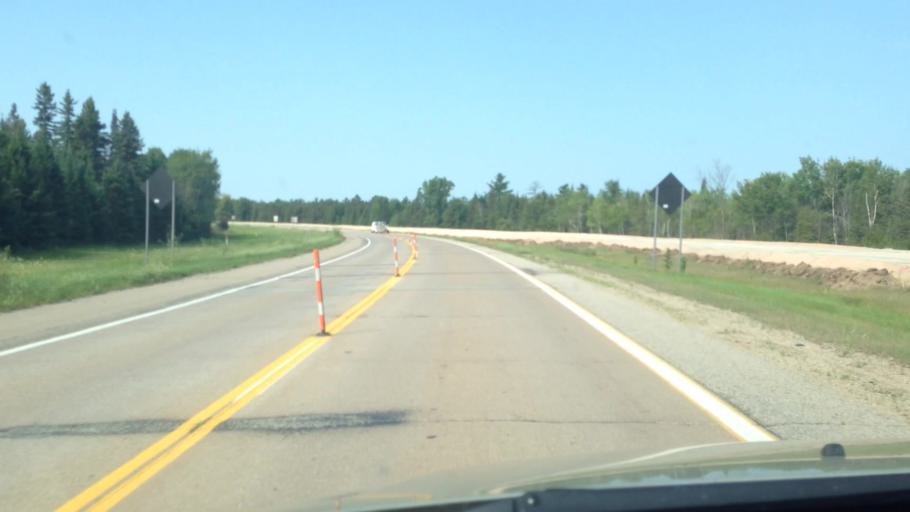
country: US
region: Michigan
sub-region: Delta County
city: Gladstone
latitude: 45.9252
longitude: -86.9861
